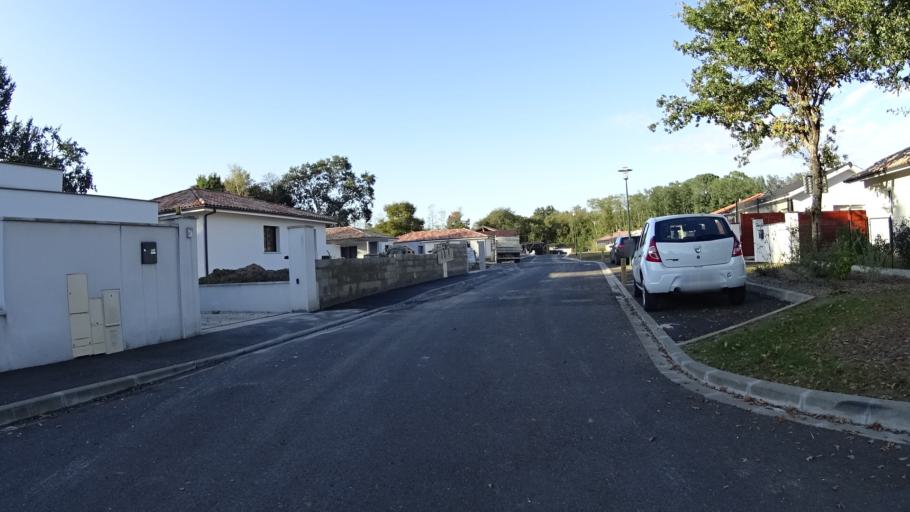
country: FR
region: Aquitaine
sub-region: Departement des Landes
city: Saint-Paul-les-Dax
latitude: 43.7407
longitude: -1.0469
